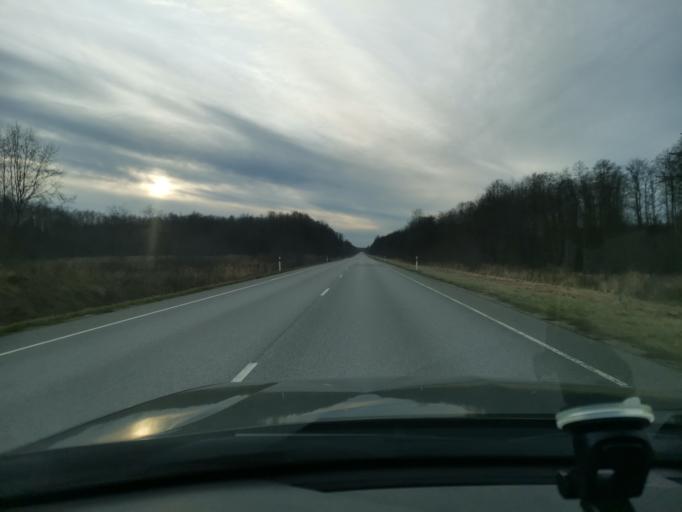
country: EE
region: Ida-Virumaa
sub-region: Narva-Joesuu linn
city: Narva-Joesuu
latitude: 59.3344
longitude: 27.9605
